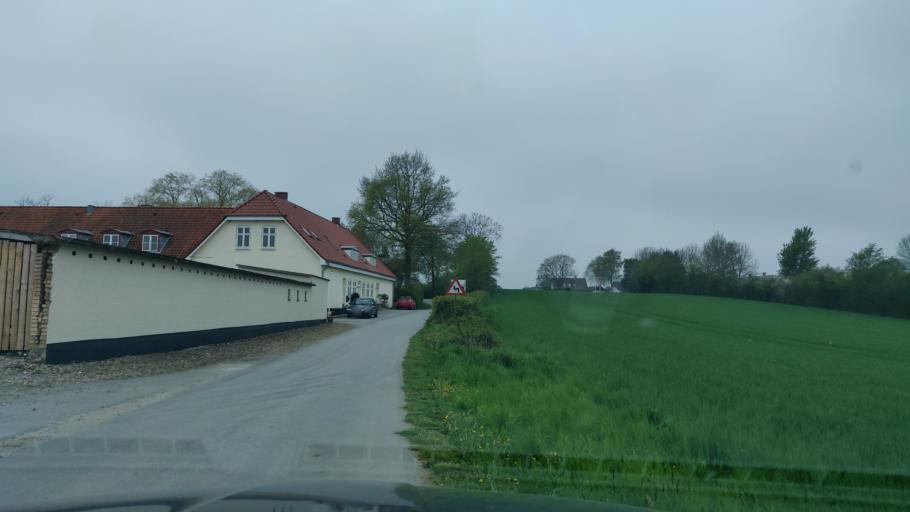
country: DK
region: South Denmark
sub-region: Sonderborg Kommune
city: Guderup
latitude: 54.9949
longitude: 9.8977
